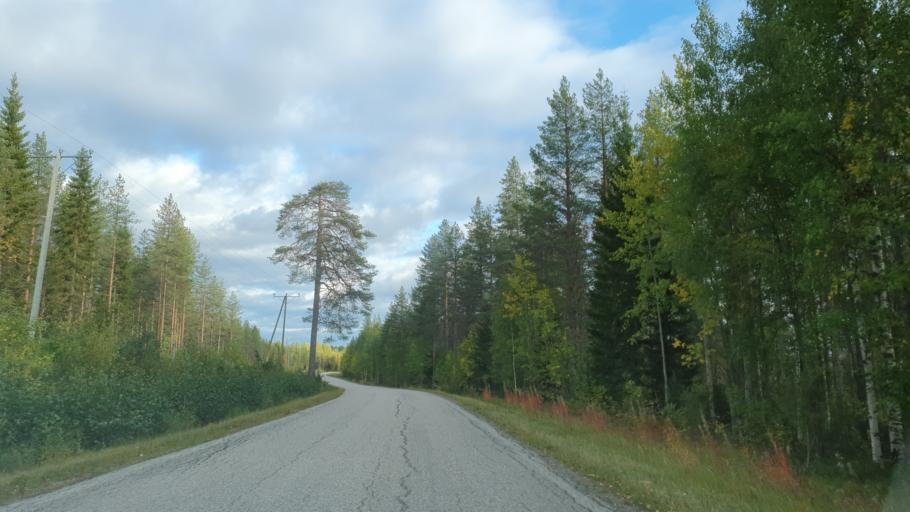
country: FI
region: Kainuu
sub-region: Kehys-Kainuu
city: Kuhmo
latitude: 63.9221
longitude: 30.0462
